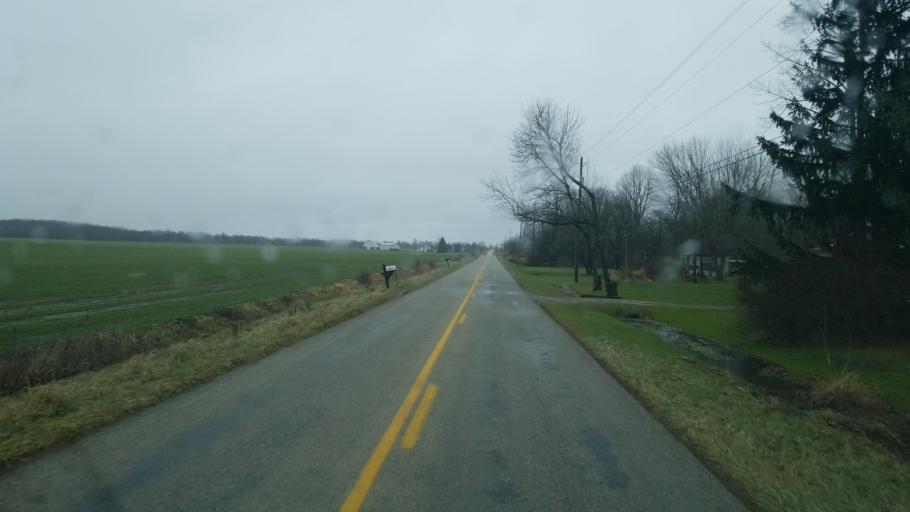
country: US
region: Ohio
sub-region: Ashtabula County
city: Roaming Shores
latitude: 41.5889
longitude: -80.7299
